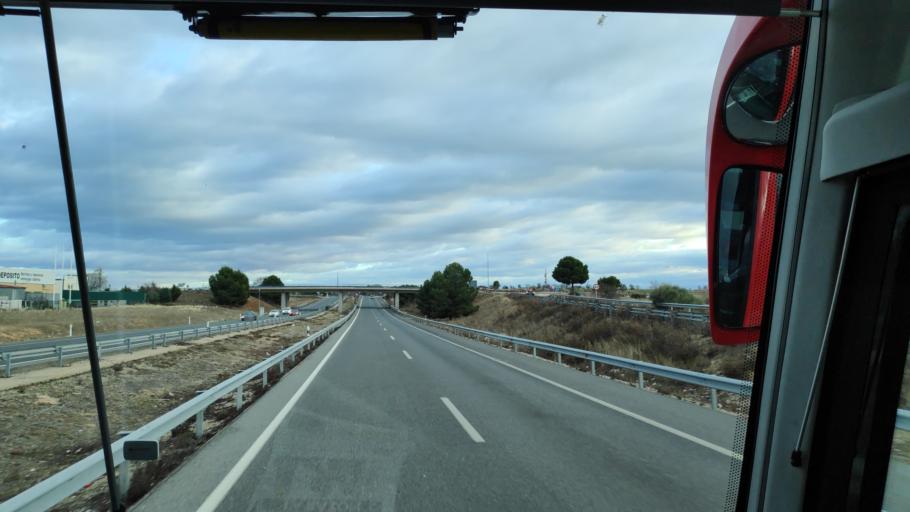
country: ES
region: Madrid
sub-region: Provincia de Madrid
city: Villarejo de Salvanes
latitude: 40.1731
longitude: -3.2939
